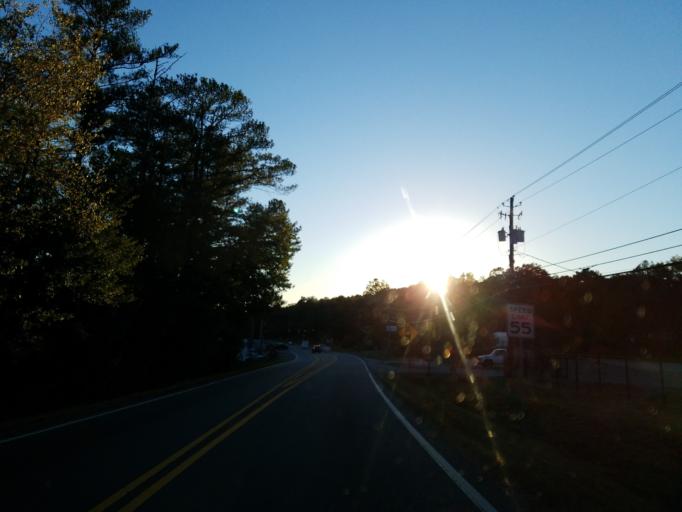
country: US
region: Georgia
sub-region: Forsyth County
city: Cumming
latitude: 34.2506
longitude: -84.1102
